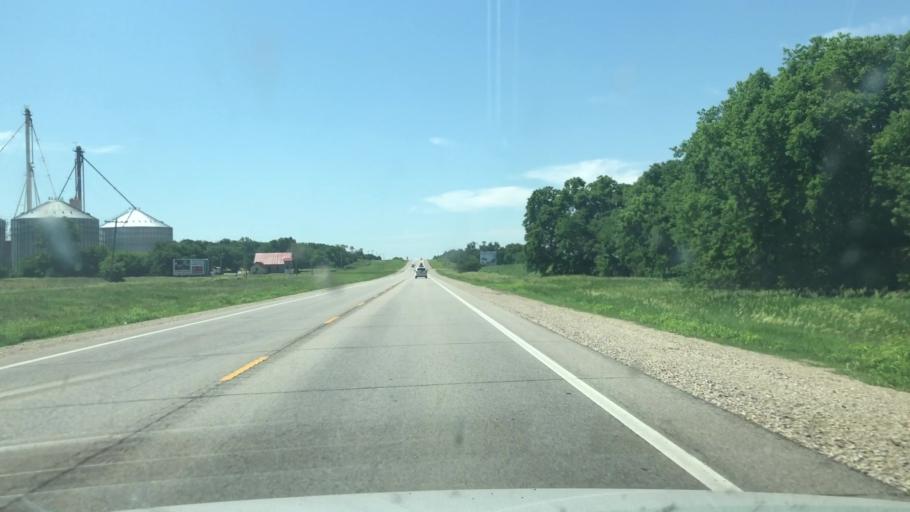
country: US
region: Kansas
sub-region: Cowley County
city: Winfield
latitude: 37.3790
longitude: -97.0070
